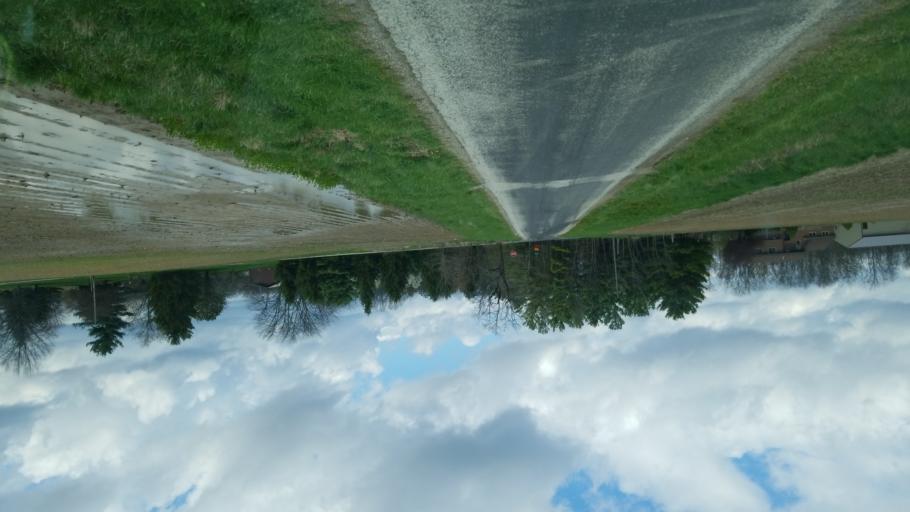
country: US
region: Ohio
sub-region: Union County
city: Richwood
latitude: 40.3637
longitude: -83.2371
